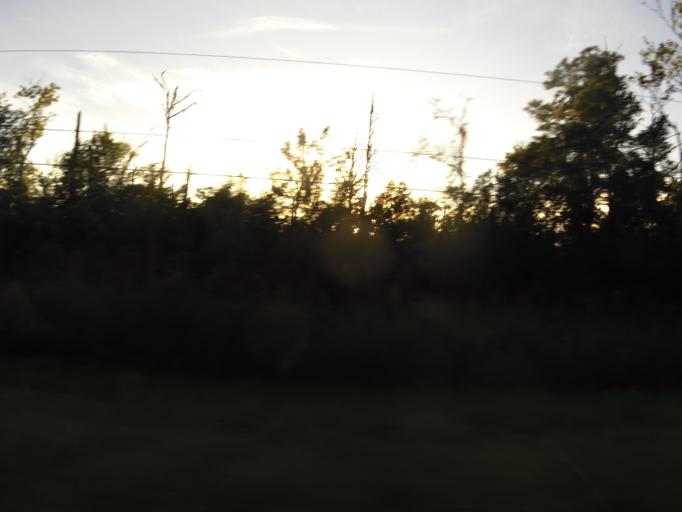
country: US
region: Georgia
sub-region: Camden County
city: Woodbine
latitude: 31.0840
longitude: -81.7265
